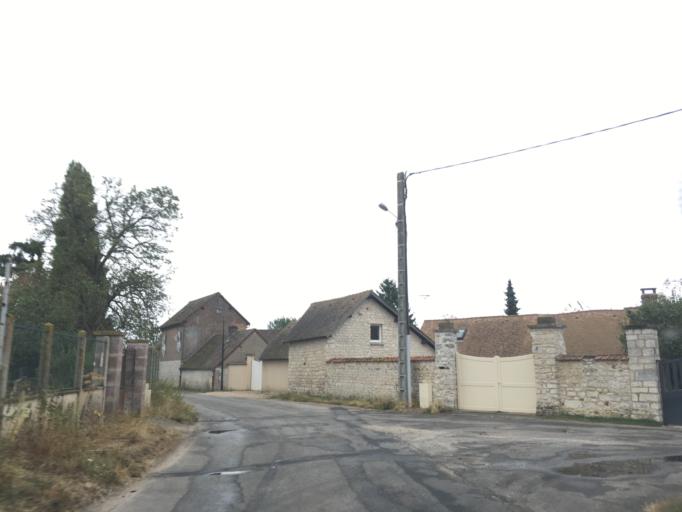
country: FR
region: Ile-de-France
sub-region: Departement des Yvelines
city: Limetz-Villez
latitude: 49.1018
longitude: 1.5406
